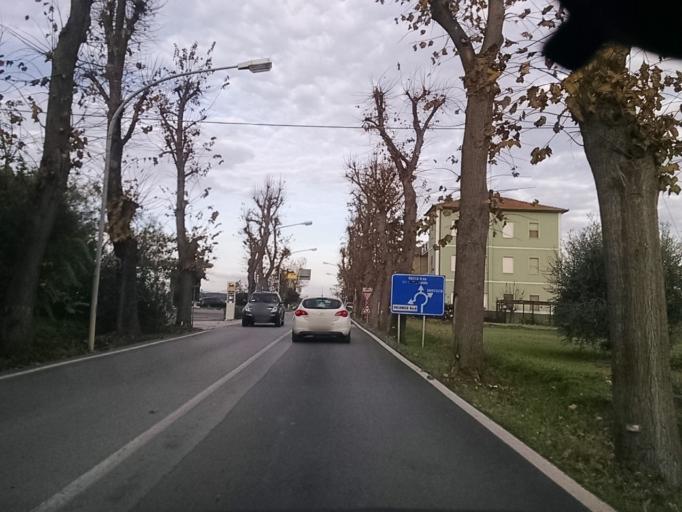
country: IT
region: Tuscany
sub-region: Provincia di Grosseto
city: Follonica
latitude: 42.9344
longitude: 10.7753
